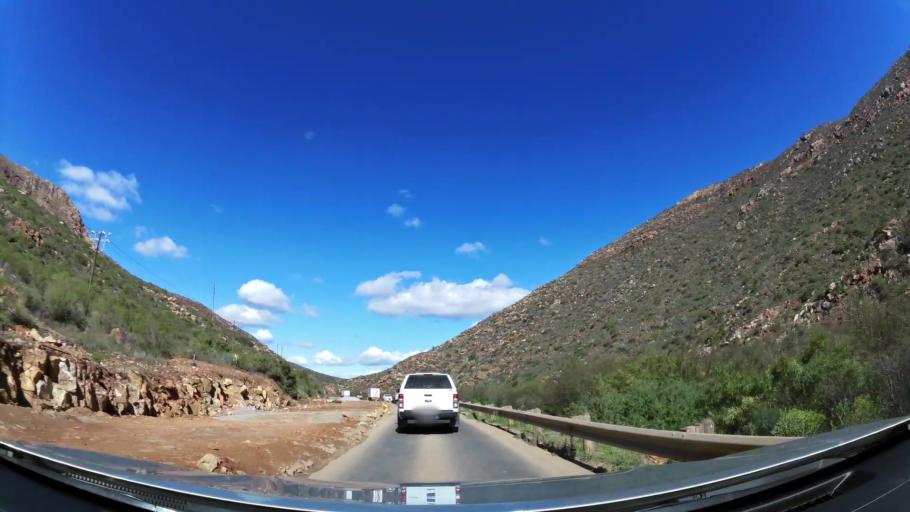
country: ZA
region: Western Cape
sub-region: Cape Winelands District Municipality
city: Ashton
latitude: -33.8150
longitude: 20.0900
